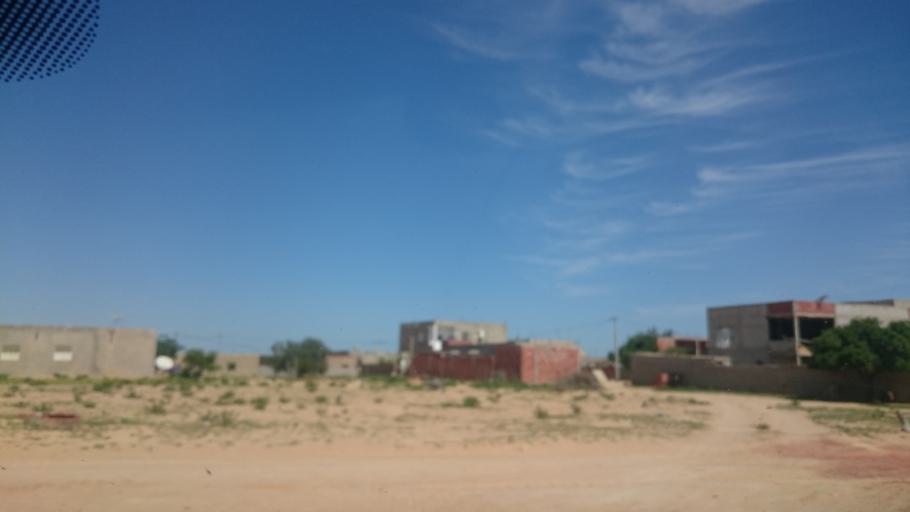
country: TN
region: Safaqis
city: Sfax
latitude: 34.7481
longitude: 10.5144
